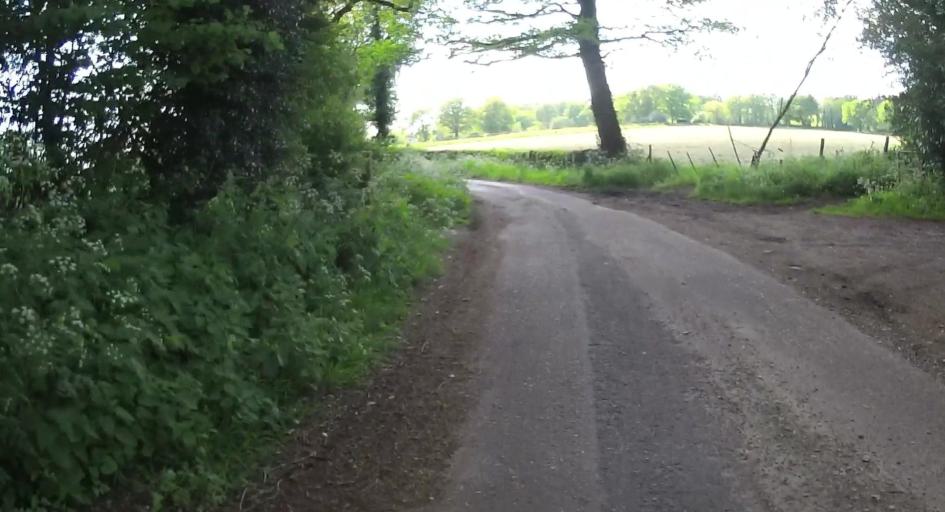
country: GB
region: England
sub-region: Surrey
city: Farnham
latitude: 51.1740
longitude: -0.8044
